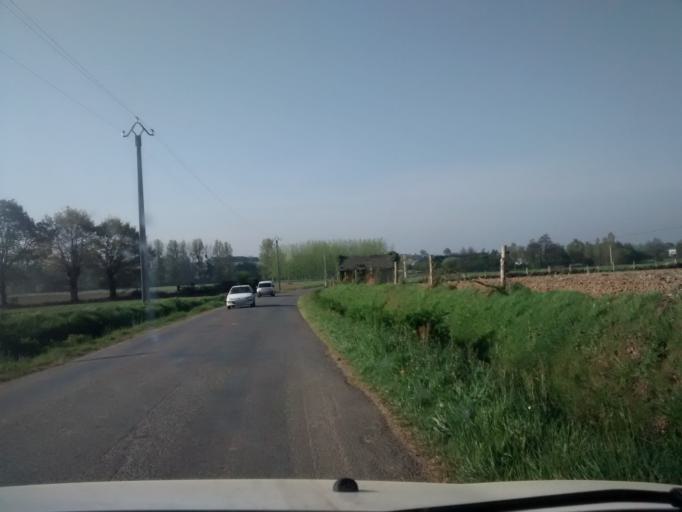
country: FR
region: Brittany
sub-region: Departement d'Ille-et-Vilaine
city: Saint-Sauveur-des-Landes
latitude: 48.3050
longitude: -1.3082
